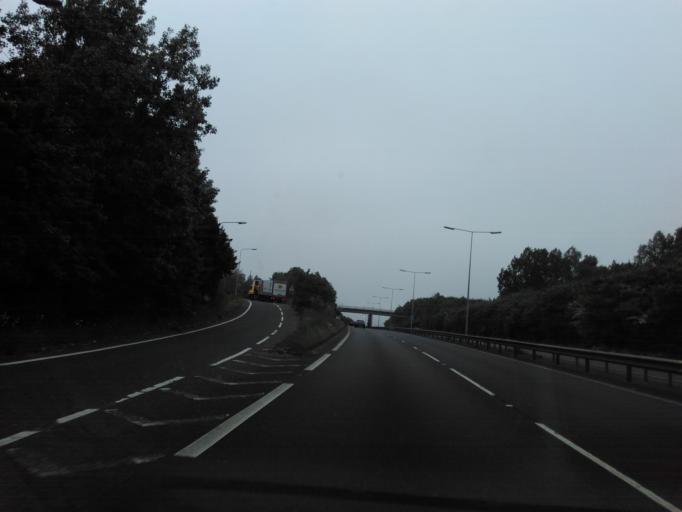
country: GB
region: England
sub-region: Kent
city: Dunkirk
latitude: 51.3144
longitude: 0.9551
